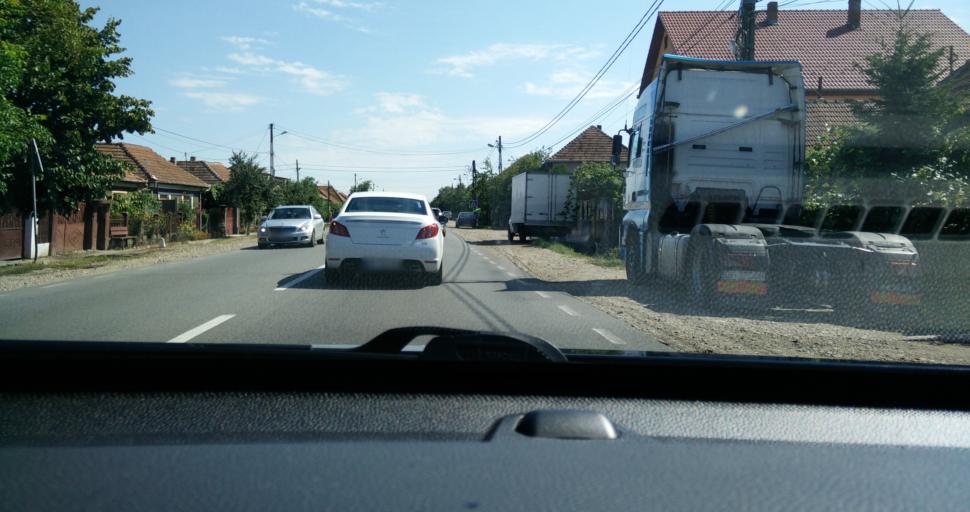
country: RO
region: Bihor
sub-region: Comuna Osorheiu
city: Alparea
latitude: 47.0379
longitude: 22.0149
